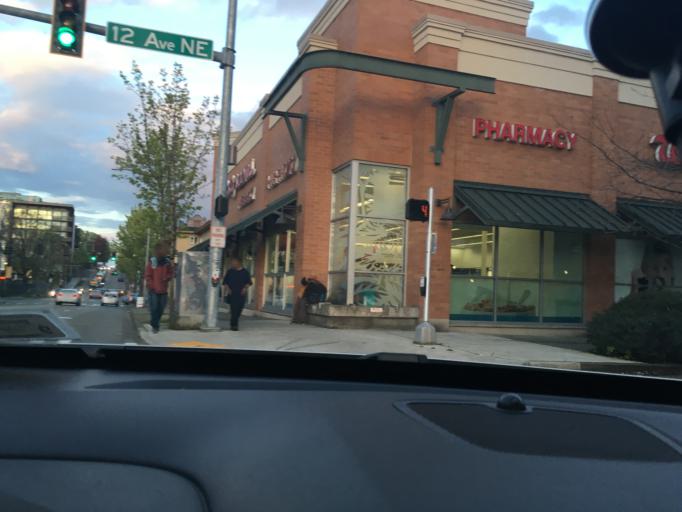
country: US
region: Washington
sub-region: King County
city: Seattle
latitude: 47.6649
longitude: -122.3154
